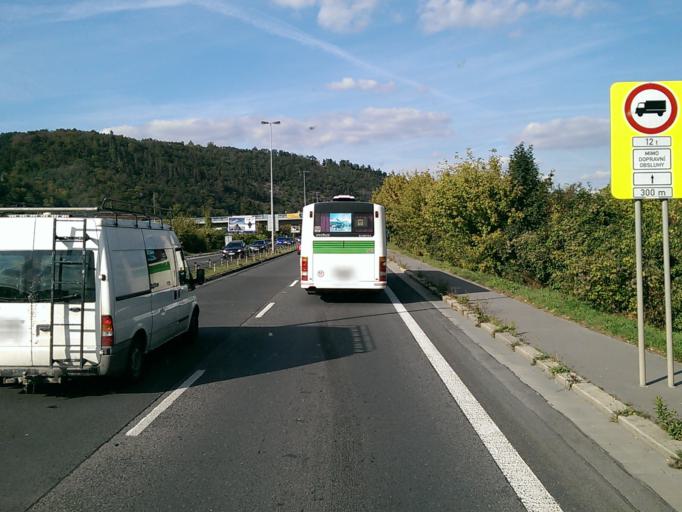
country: CZ
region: Praha
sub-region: Praha 12
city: Modrany
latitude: 50.0200
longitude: 14.3942
